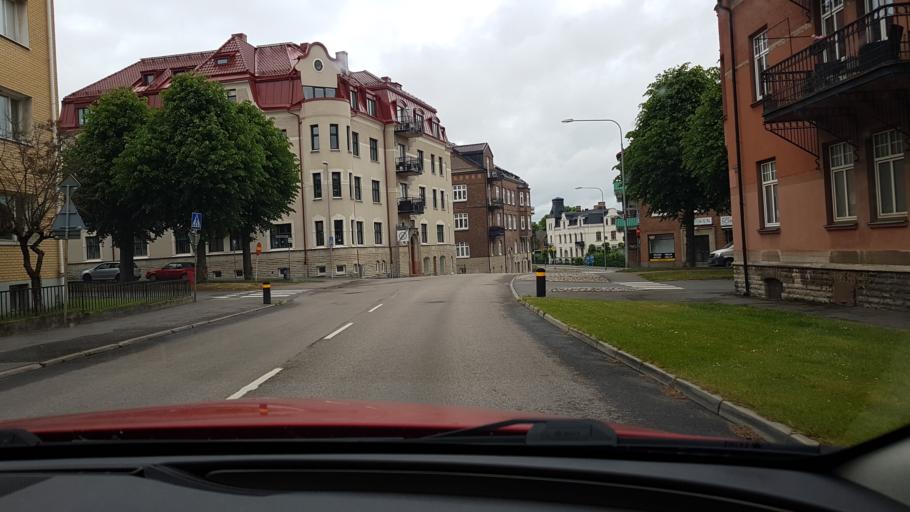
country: SE
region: Vaestra Goetaland
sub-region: Skovde Kommun
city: Skoevde
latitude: 58.3834
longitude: 13.8437
